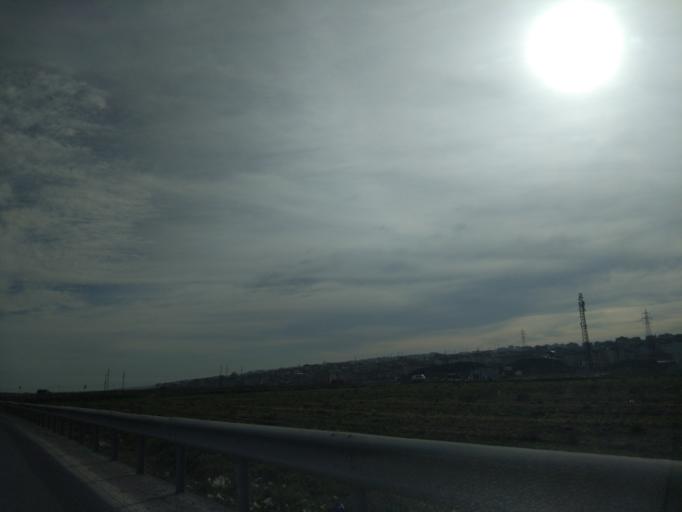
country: TR
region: Istanbul
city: Esenyurt
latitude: 41.0453
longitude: 28.7049
